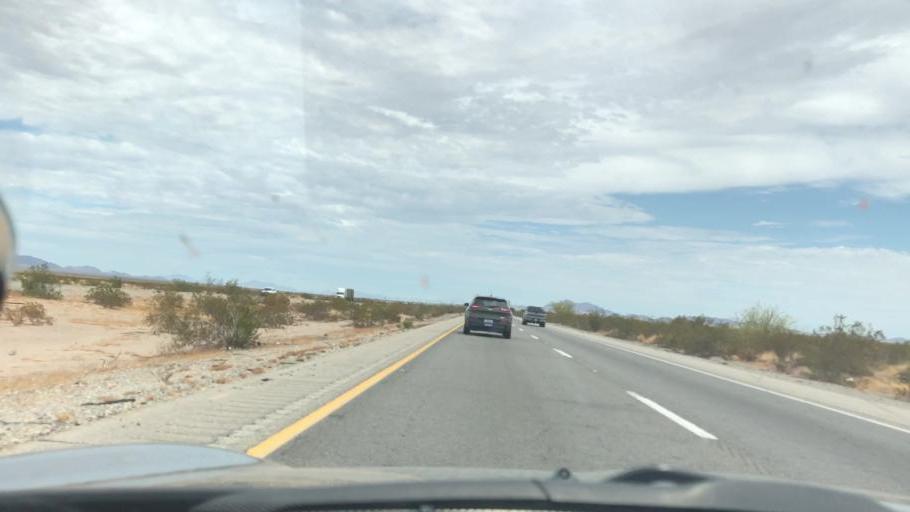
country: US
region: California
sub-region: Riverside County
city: Mesa Verde
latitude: 33.6130
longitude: -115.0099
